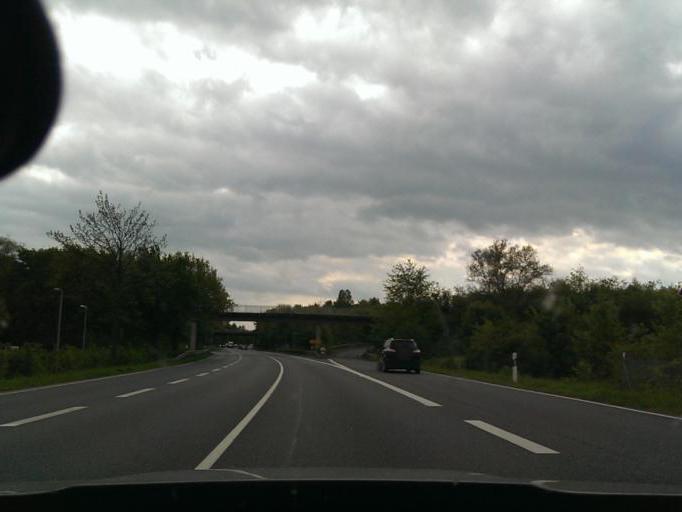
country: DE
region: Lower Saxony
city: Laatzen
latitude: 52.2970
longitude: 9.8207
